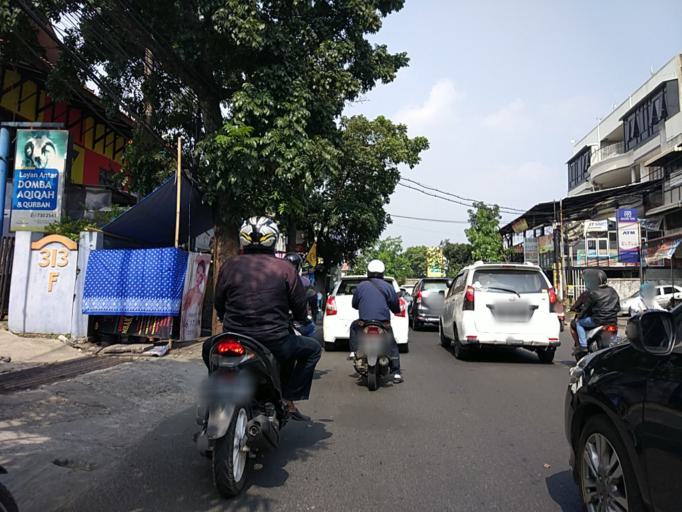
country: ID
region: West Java
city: Bandung
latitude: -6.9289
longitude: 107.6384
